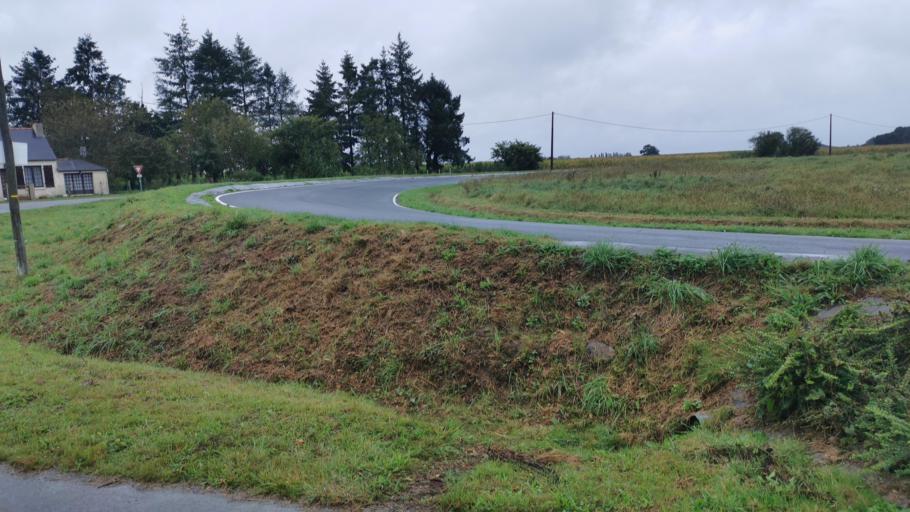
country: FR
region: Brittany
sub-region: Departement des Cotes-d'Armor
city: Pleslin-Trigavou
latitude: 48.5410
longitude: -2.0438
